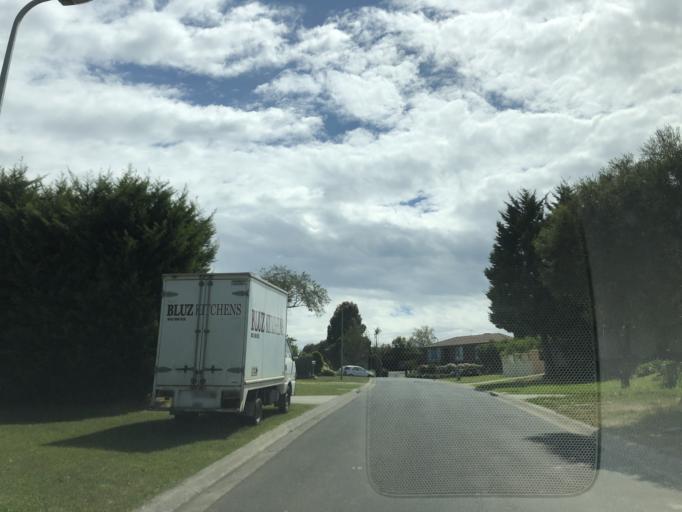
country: AU
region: Victoria
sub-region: Casey
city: Endeavour Hills
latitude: -37.9667
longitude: 145.2690
